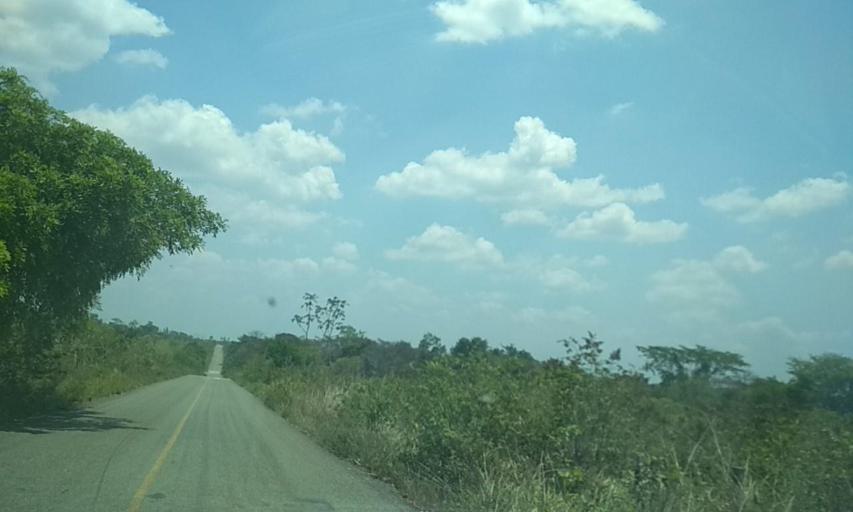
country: MX
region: Tabasco
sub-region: Huimanguillo
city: Francisco Rueda
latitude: 17.8222
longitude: -93.8716
